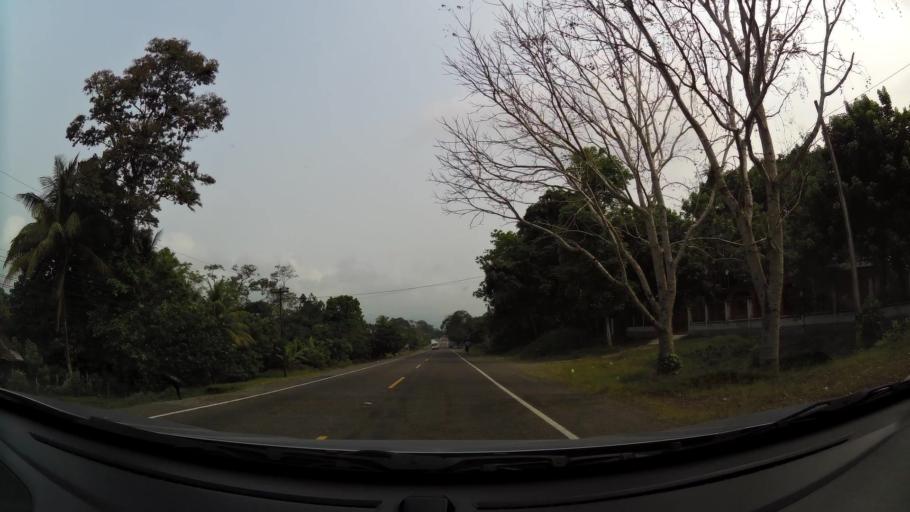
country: HN
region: Atlantida
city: Mezapa
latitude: 15.6006
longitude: -87.6100
